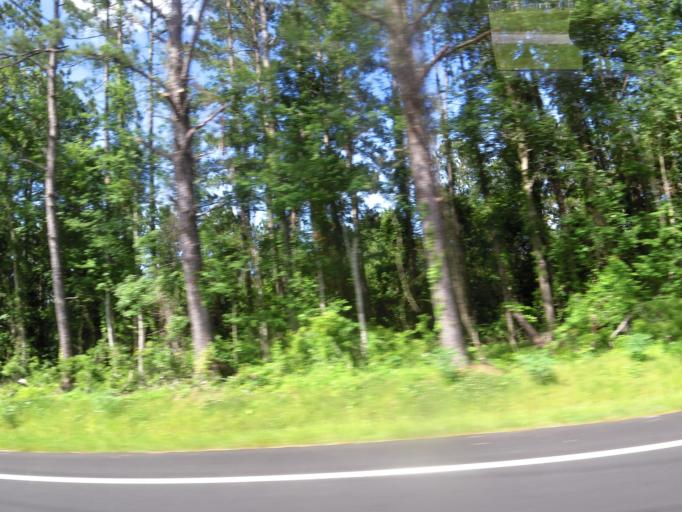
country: US
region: Florida
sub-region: Nassau County
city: Hilliard
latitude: 30.6685
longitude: -81.9054
